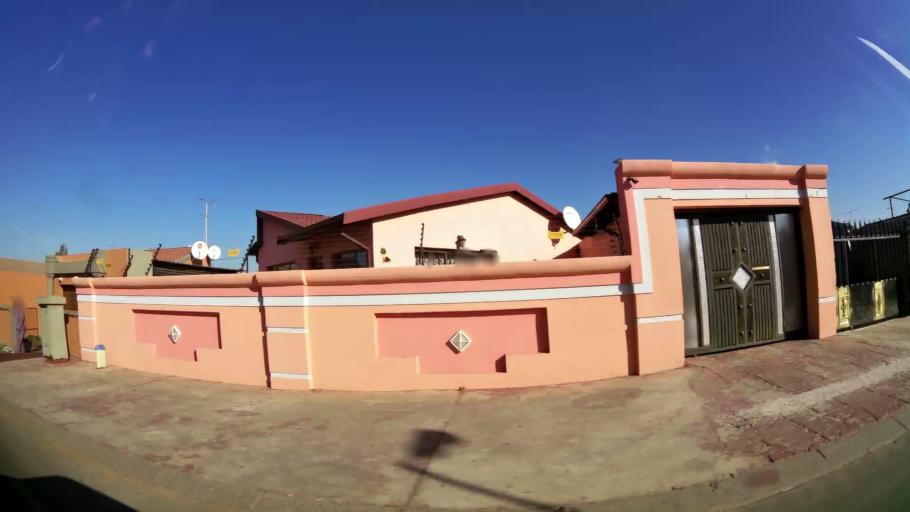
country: ZA
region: Gauteng
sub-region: City of Johannesburg Metropolitan Municipality
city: Roodepoort
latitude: -26.1571
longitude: 27.8485
